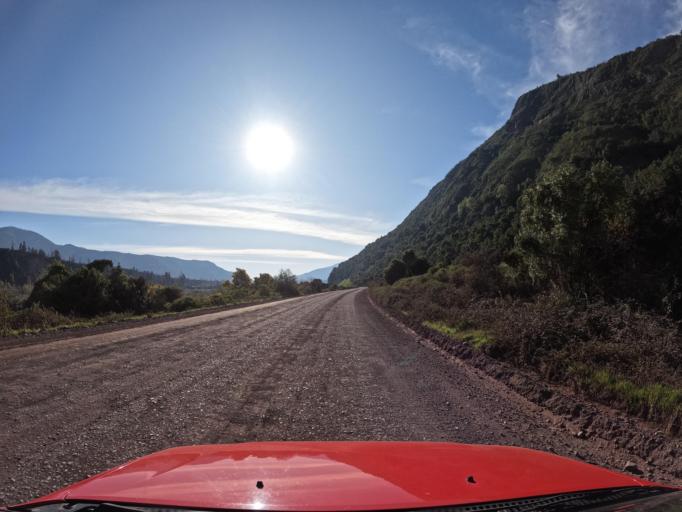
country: CL
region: Maule
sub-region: Provincia de Curico
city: Teno
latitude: -35.0003
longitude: -70.8415
